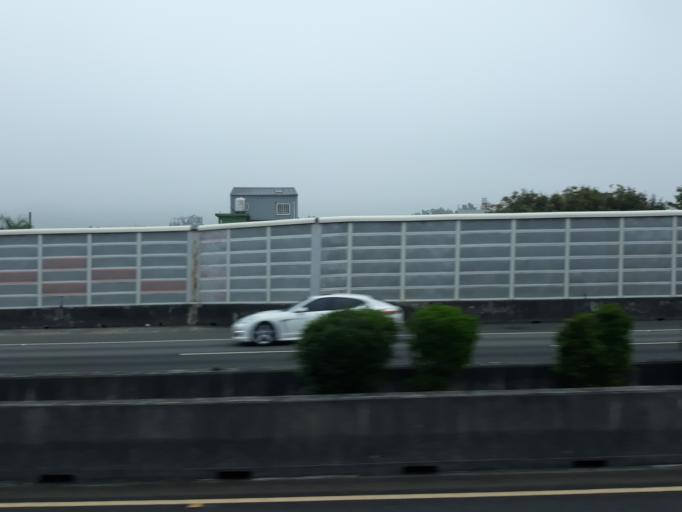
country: TW
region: Taiwan
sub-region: Miaoli
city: Miaoli
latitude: 24.5358
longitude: 120.8288
